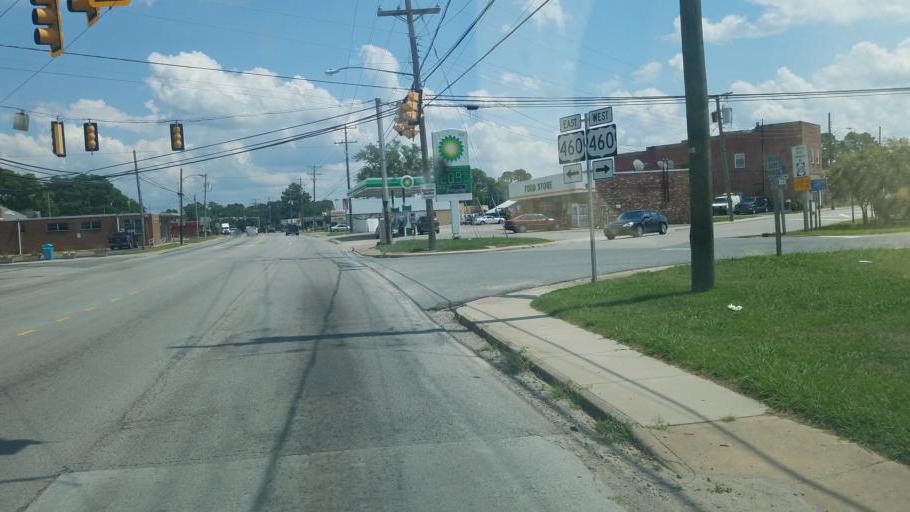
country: US
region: Virginia
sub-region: Isle of Wight County
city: Windsor
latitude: 36.8085
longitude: -76.7444
